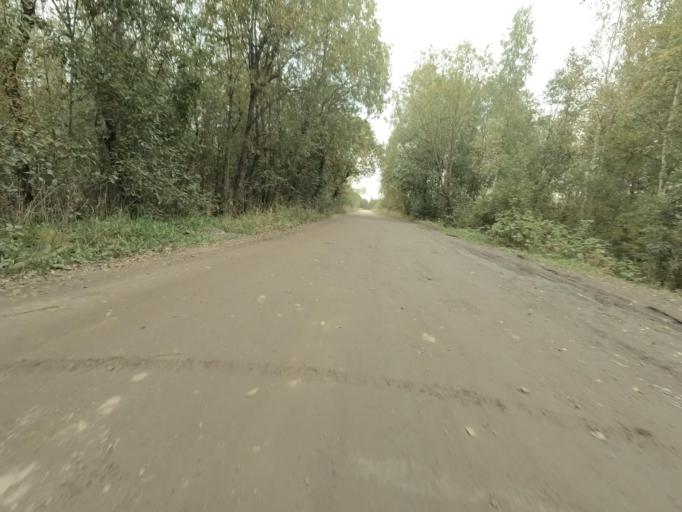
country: RU
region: St.-Petersburg
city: Sapernyy
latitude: 59.7603
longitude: 30.6545
